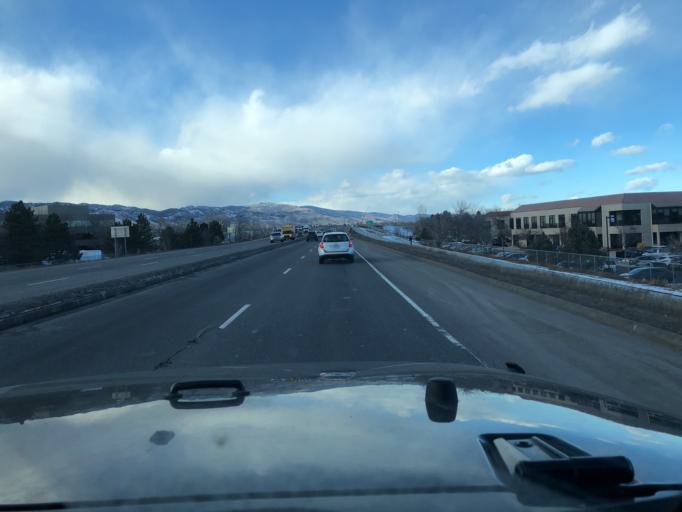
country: US
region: Colorado
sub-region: Boulder County
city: Boulder
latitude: 40.0169
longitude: -105.2421
